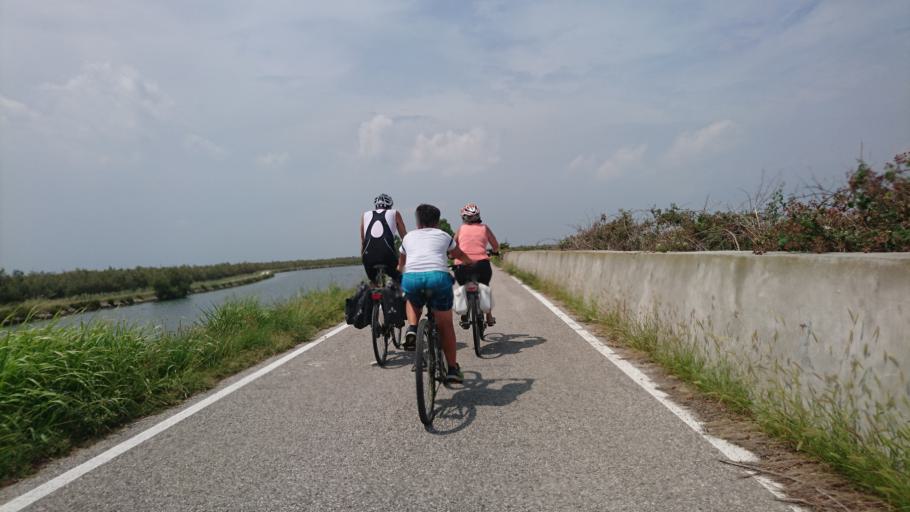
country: IT
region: Veneto
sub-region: Provincia di Rovigo
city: Rosolina
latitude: 45.0651
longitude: 12.3140
